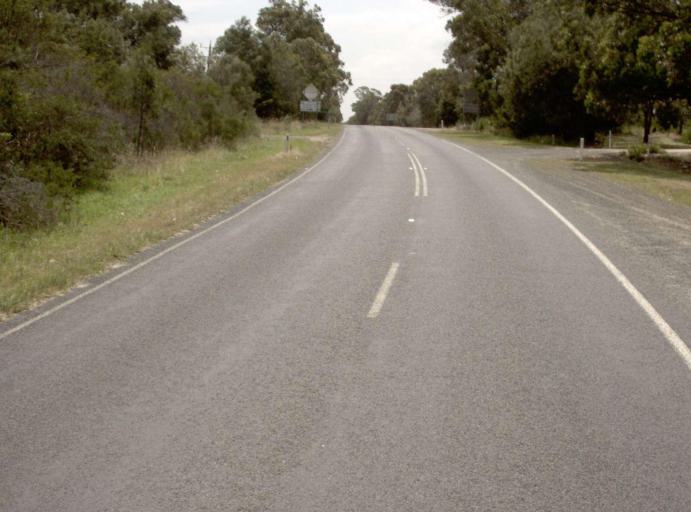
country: AU
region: Victoria
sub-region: Latrobe
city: Traralgon
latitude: -38.5451
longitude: 146.7016
